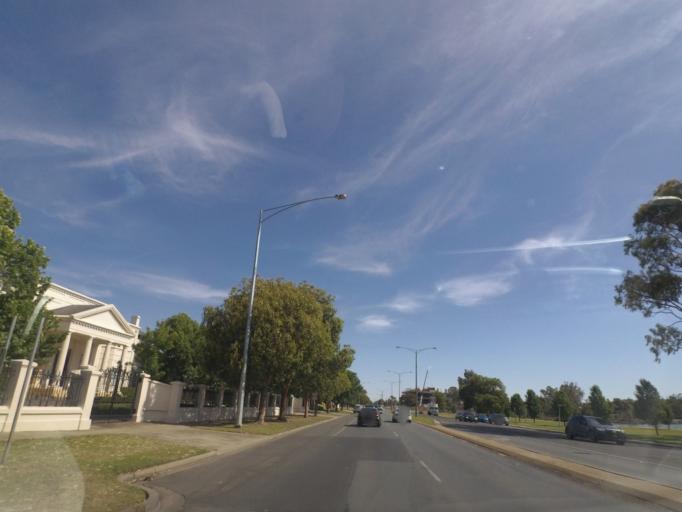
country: AU
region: Victoria
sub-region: Greater Shepparton
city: Shepparton
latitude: -36.3878
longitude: 145.3980
